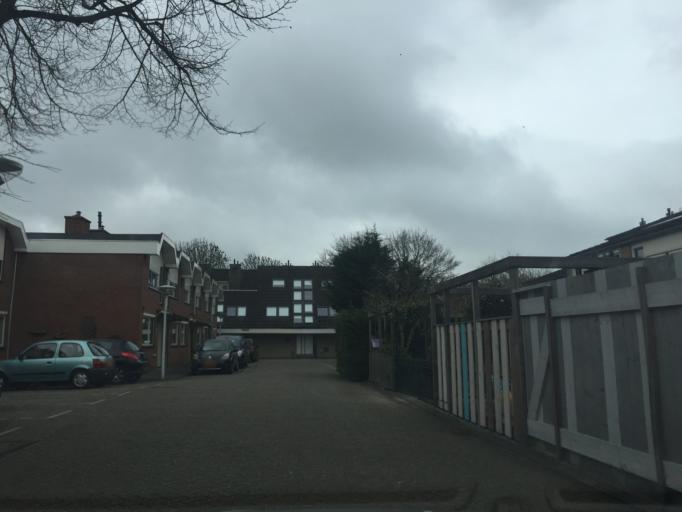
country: NL
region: South Holland
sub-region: Gemeente Leiden
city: Leiden
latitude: 52.1782
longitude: 4.5028
